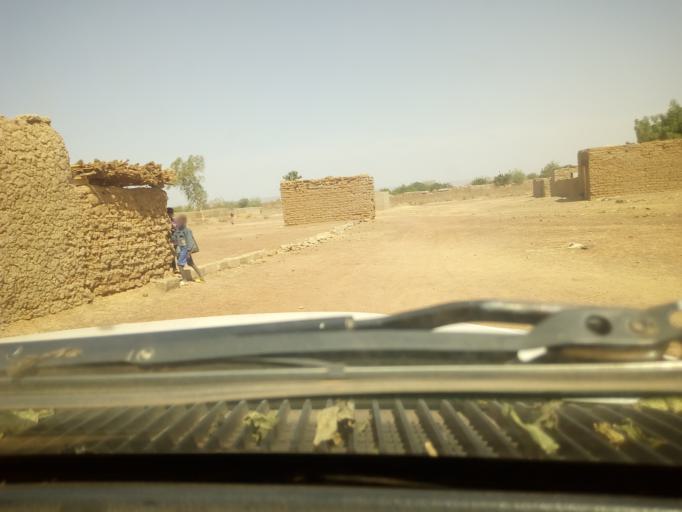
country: ML
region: Koulikoro
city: Koulikoro
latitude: 12.6475
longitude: -7.7085
